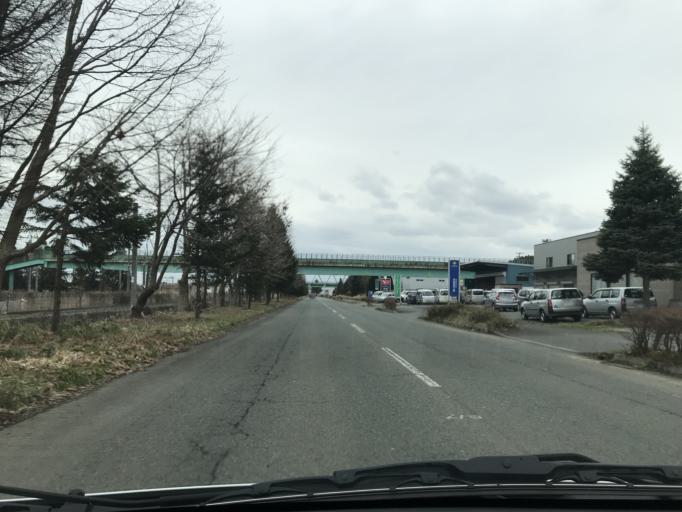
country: JP
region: Iwate
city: Kitakami
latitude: 39.2642
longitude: 141.1130
